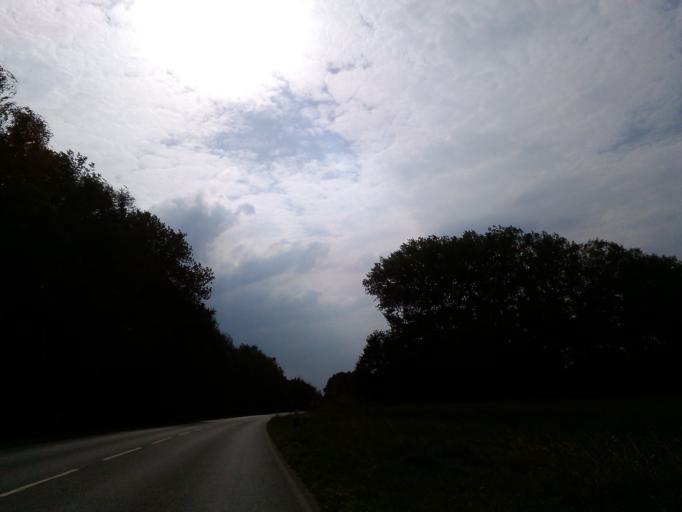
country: DE
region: Bavaria
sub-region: Upper Bavaria
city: Puchheim
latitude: 48.1646
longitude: 11.3530
